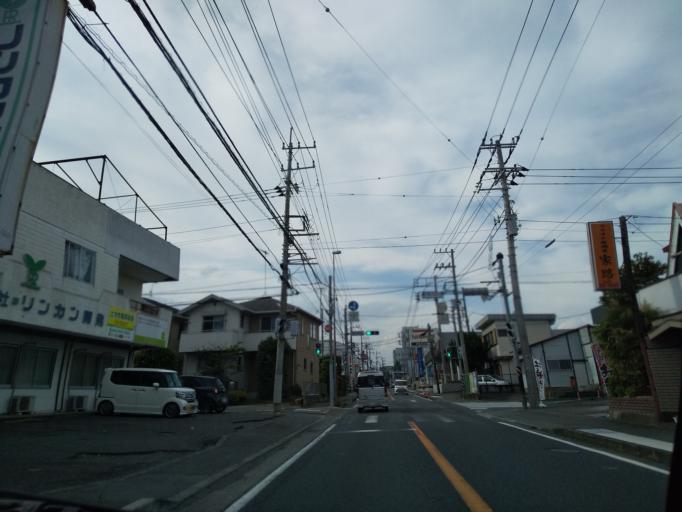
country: JP
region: Kanagawa
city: Atsugi
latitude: 35.4814
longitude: 139.3414
